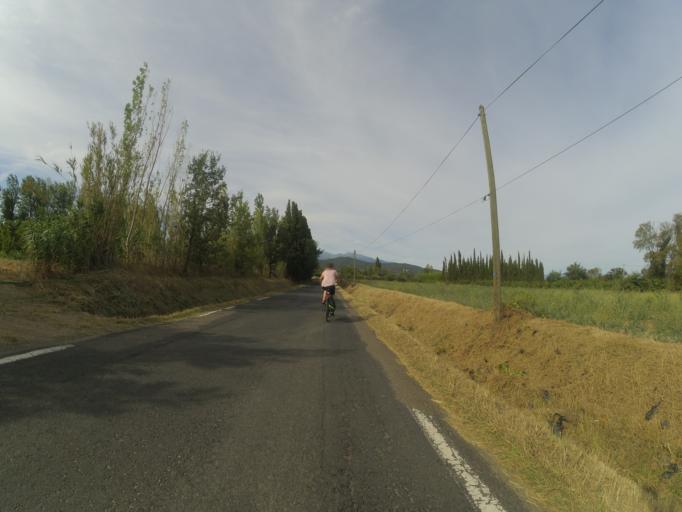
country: FR
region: Languedoc-Roussillon
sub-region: Departement des Pyrenees-Orientales
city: Millas
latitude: 42.6641
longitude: 2.6897
